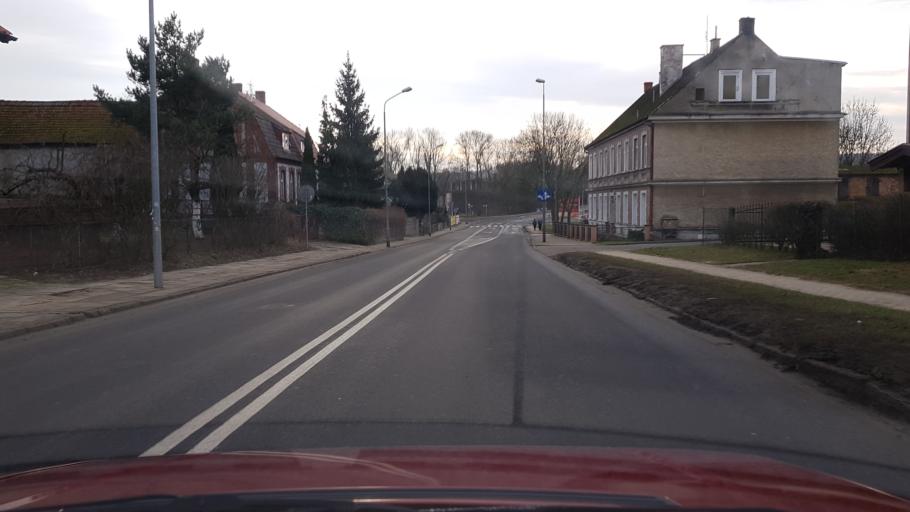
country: PL
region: West Pomeranian Voivodeship
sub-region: Powiat policki
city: Police
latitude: 53.5458
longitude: 14.5747
